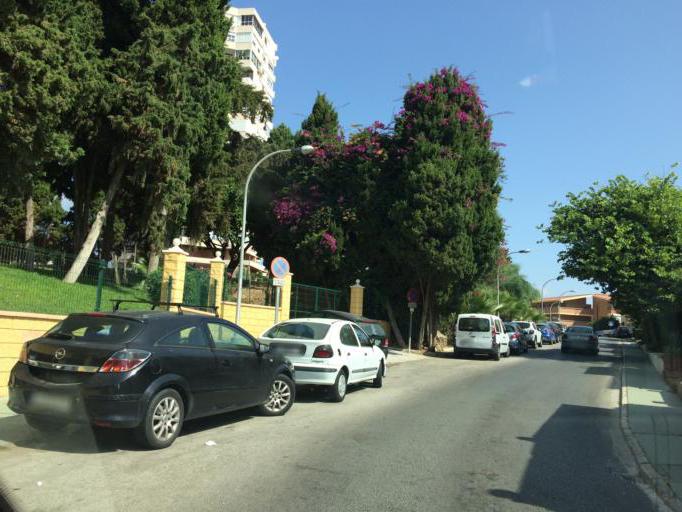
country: ES
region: Andalusia
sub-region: Provincia de Malaga
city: Torremolinos
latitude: 36.6384
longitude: -4.4933
